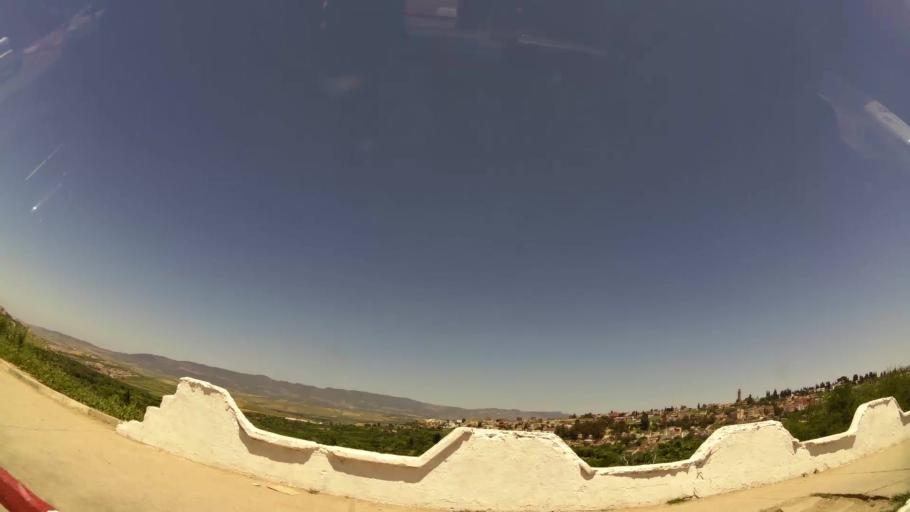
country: MA
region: Meknes-Tafilalet
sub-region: Meknes
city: Meknes
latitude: 33.9040
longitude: -5.5714
